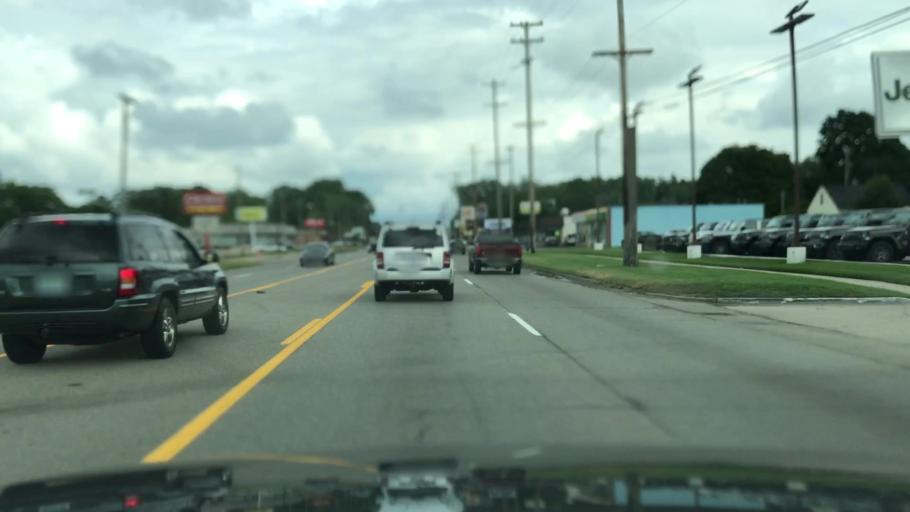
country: US
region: Michigan
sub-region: Kent County
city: Kentwood
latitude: 42.9128
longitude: -85.6552
